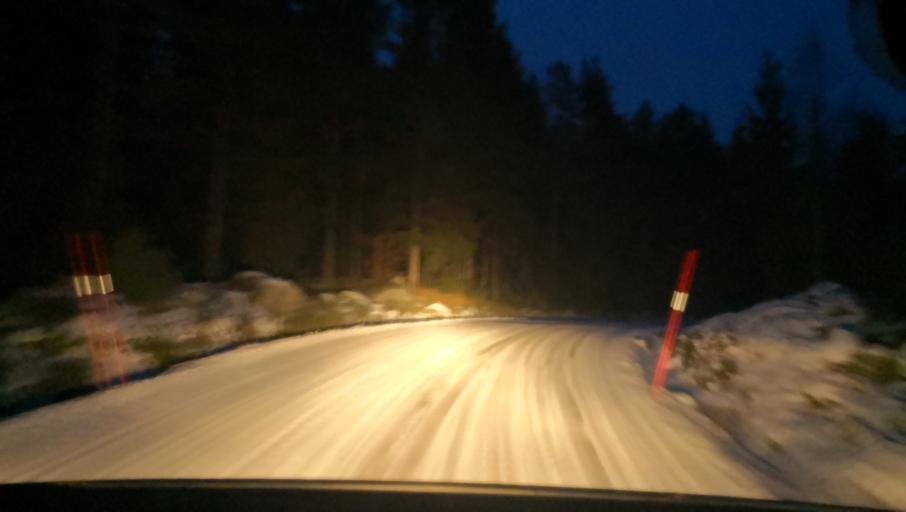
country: SE
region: Uppsala
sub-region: Heby Kommun
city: Tarnsjo
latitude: 60.2523
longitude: 16.7538
